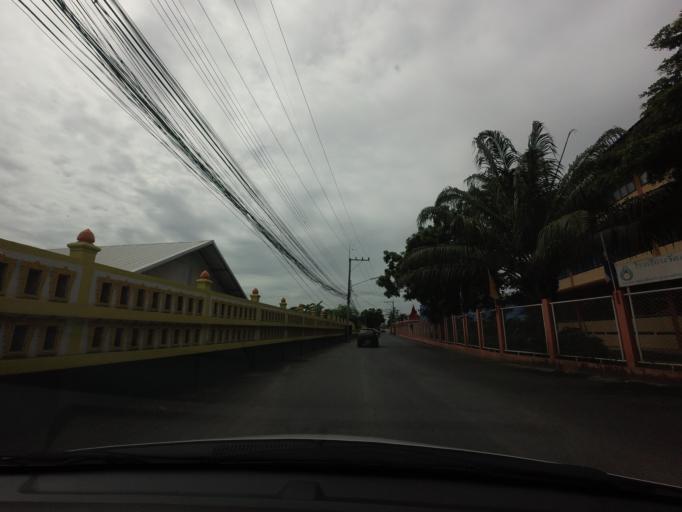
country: TH
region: Pathum Thani
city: Lam Luk Ka
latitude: 13.9296
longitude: 100.7132
